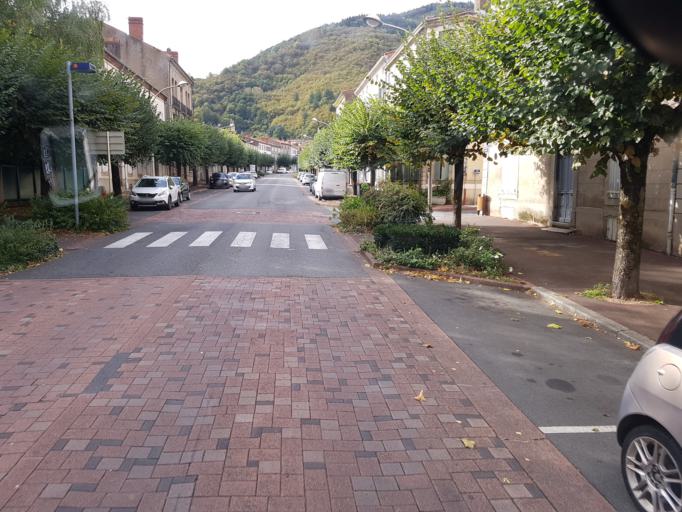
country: FR
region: Midi-Pyrenees
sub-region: Departement du Tarn
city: Mazamet
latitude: 43.4884
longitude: 2.3750
